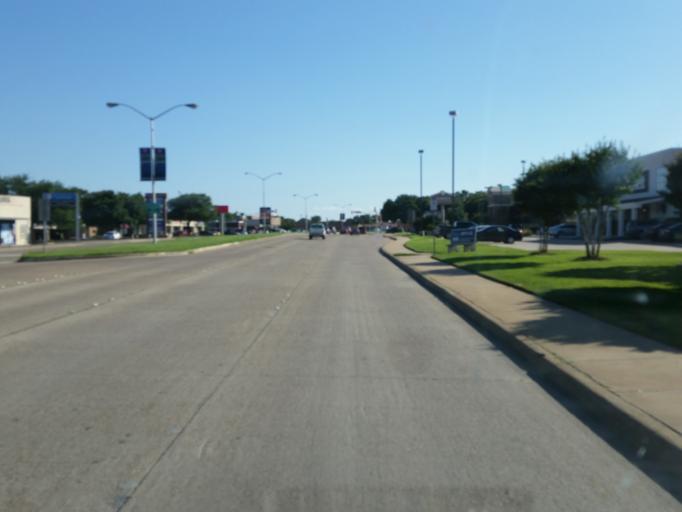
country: US
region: Texas
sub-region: Tarrant County
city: Edgecliff Village
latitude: 32.6793
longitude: -97.3943
